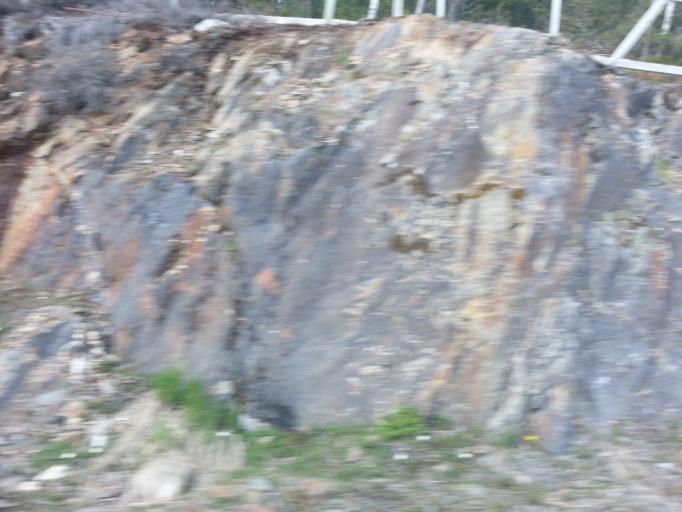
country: NO
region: Nord-Trondelag
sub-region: Levanger
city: Skogn
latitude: 63.6366
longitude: 11.2295
